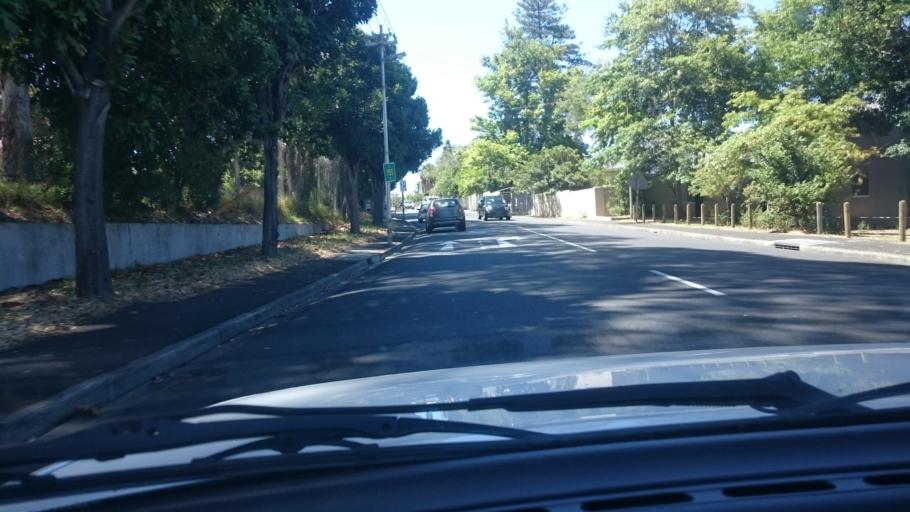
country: ZA
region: Western Cape
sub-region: City of Cape Town
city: Claremont
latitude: -34.0058
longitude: 18.4620
